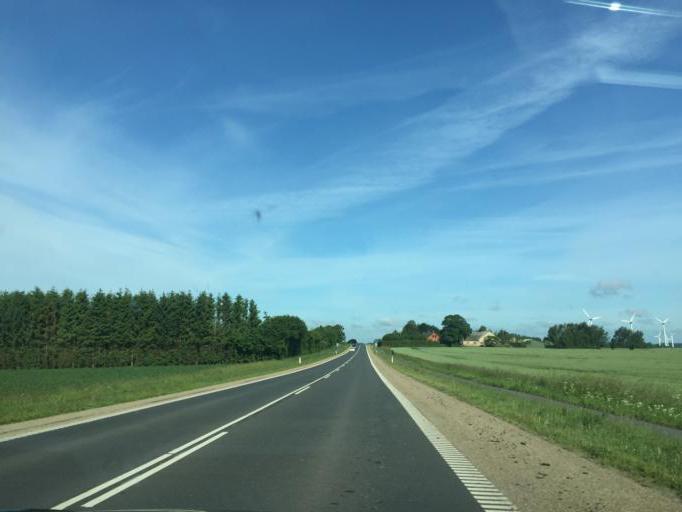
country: DK
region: South Denmark
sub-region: Middelfart Kommune
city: Norre Aby
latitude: 55.4805
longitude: 9.8440
